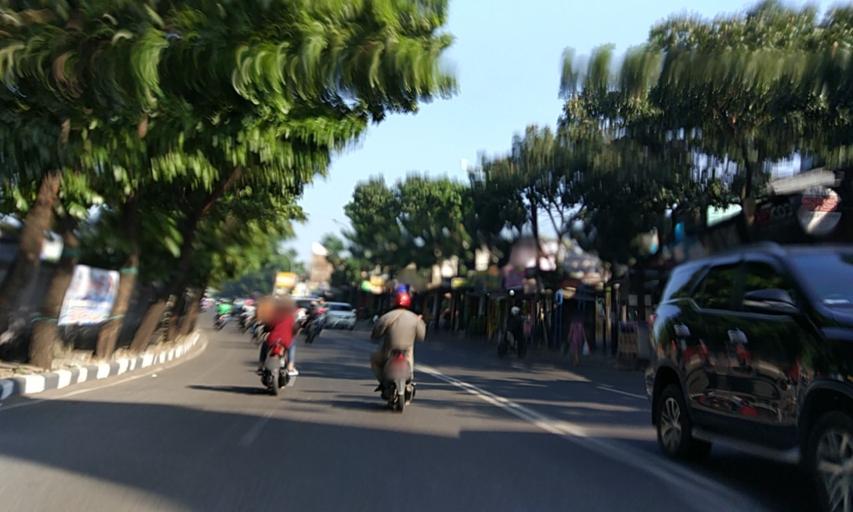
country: ID
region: West Java
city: Bandung
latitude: -6.8994
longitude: 107.6264
